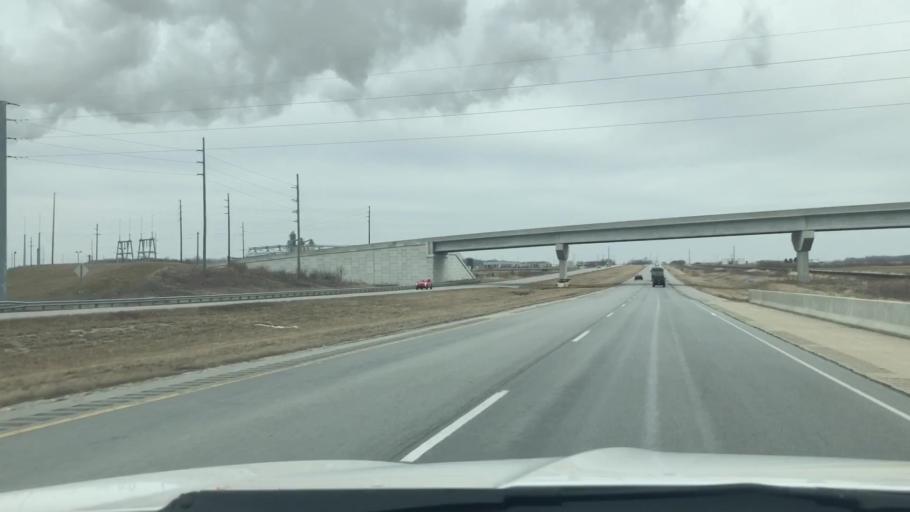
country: US
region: Indiana
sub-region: Cass County
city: Dunkirk
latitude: 40.7143
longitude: -86.4358
